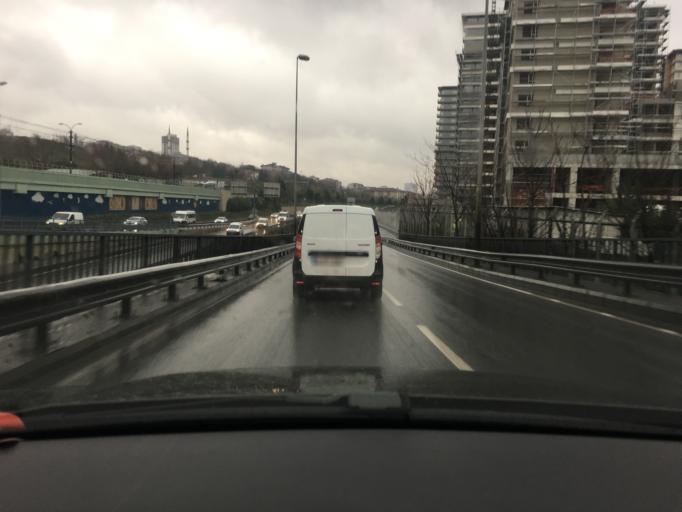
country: TR
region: Istanbul
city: merter keresteciler
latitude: 41.0218
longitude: 28.9003
